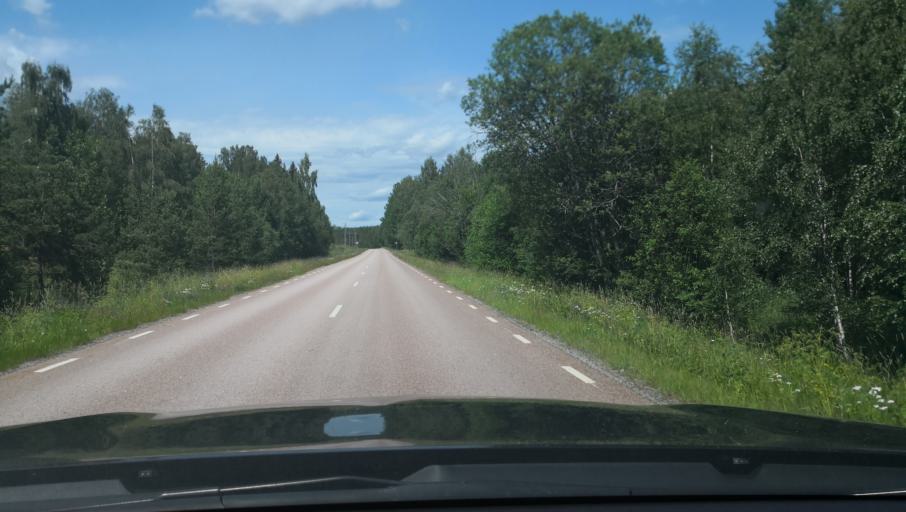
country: SE
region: Vaestmanland
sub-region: Surahammars Kommun
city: Ramnas
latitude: 59.7974
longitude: 16.1735
